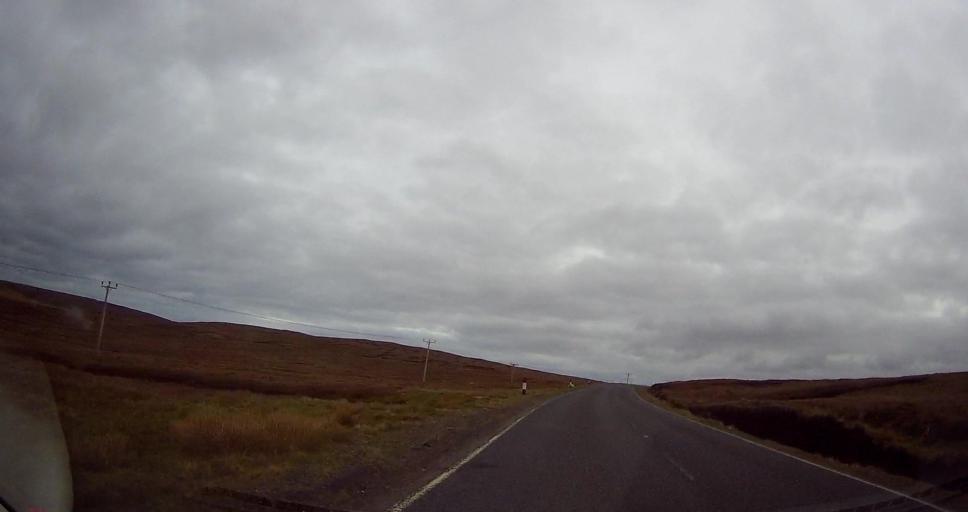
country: GB
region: Scotland
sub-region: Shetland Islands
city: Shetland
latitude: 60.6341
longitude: -1.0664
